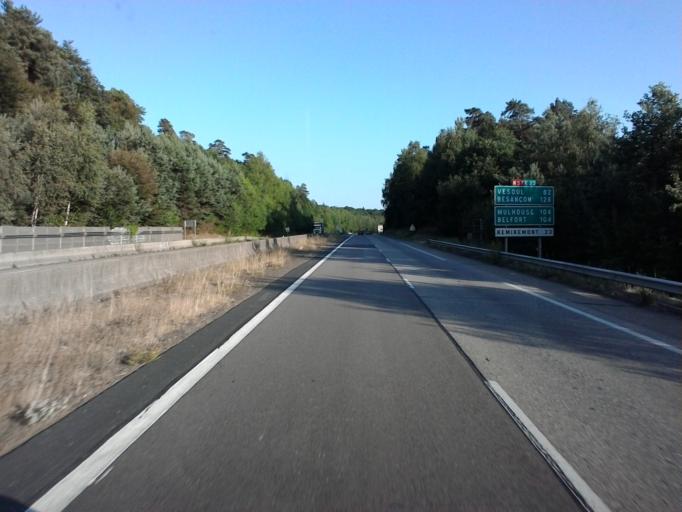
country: FR
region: Lorraine
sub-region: Departement des Vosges
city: Epinal
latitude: 48.1689
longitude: 6.4847
